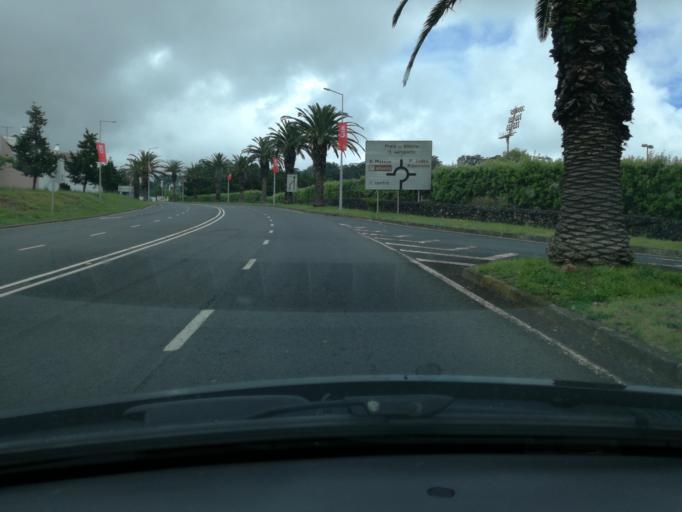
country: PT
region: Azores
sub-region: Angra do Heroismo
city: Angra do Heroismo
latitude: 38.6605
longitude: -27.2046
